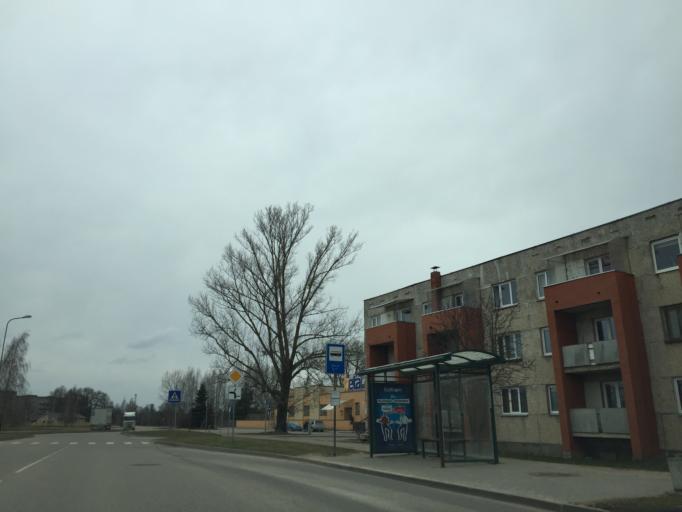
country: LV
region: Jekabpils Rajons
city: Jekabpils
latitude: 56.4931
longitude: 25.8883
